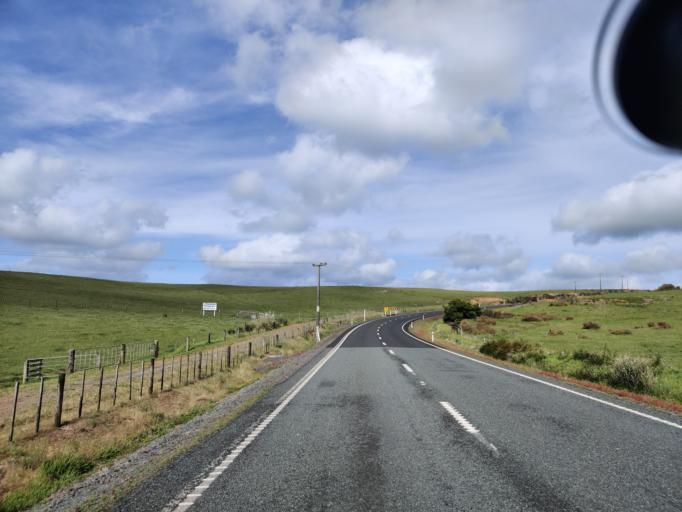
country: NZ
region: Northland
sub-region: Kaipara District
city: Dargaville
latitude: -35.7487
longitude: 173.6266
